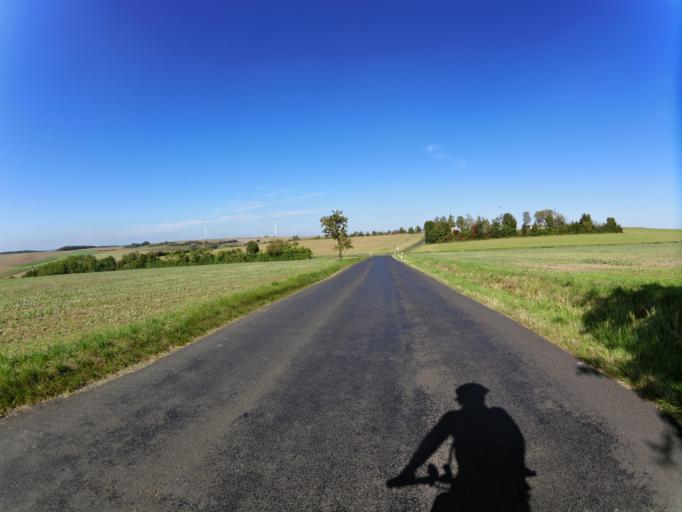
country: DE
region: Bavaria
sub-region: Regierungsbezirk Unterfranken
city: Kleinrinderfeld
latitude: 49.6993
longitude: 9.7875
